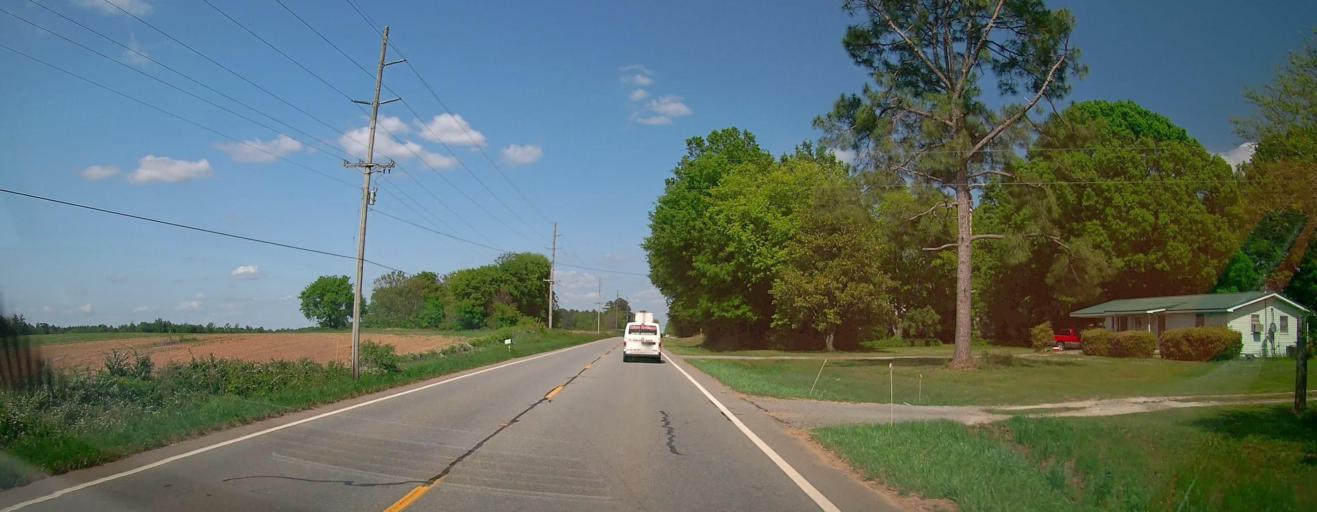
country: US
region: Georgia
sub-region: Putnam County
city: Eatonton
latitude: 33.3494
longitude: -83.3550
